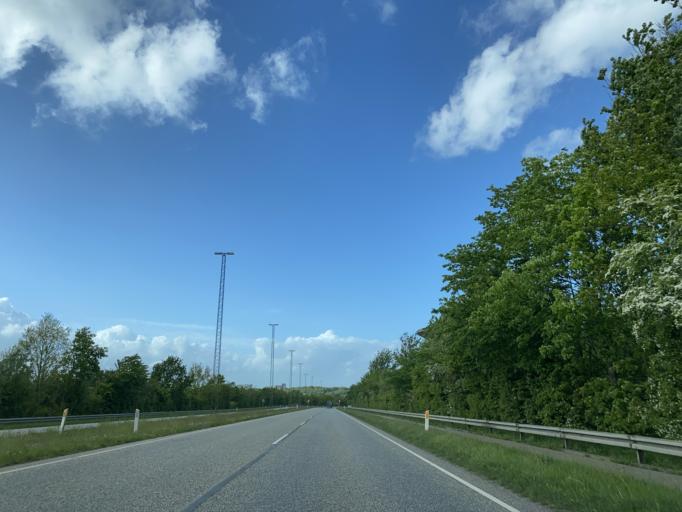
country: DK
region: Central Jutland
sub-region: Horsens Kommune
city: Horsens
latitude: 55.8504
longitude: 9.8228
